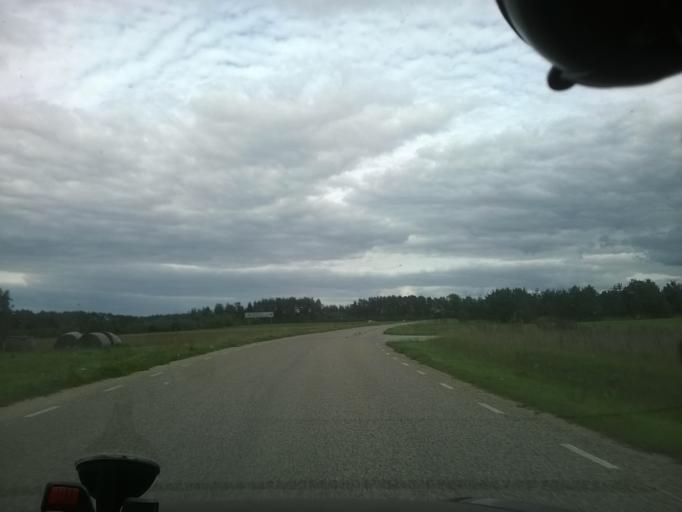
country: EE
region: Vorumaa
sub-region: Voru linn
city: Voru
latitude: 57.7477
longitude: 26.9633
